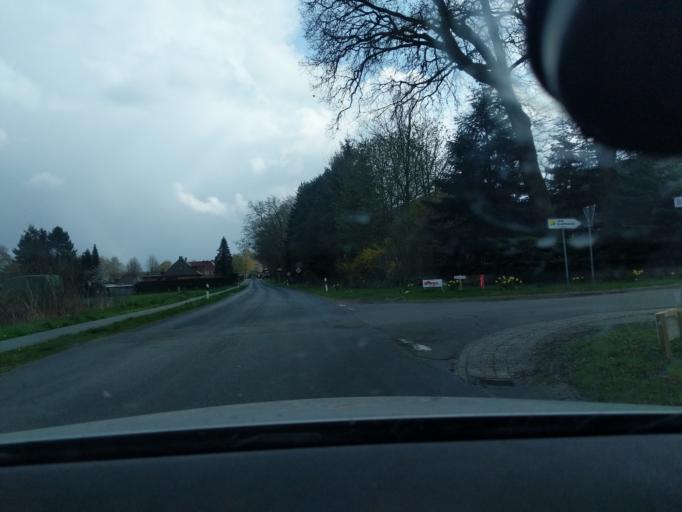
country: DE
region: Lower Saxony
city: Deinste
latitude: 53.5263
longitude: 9.4835
